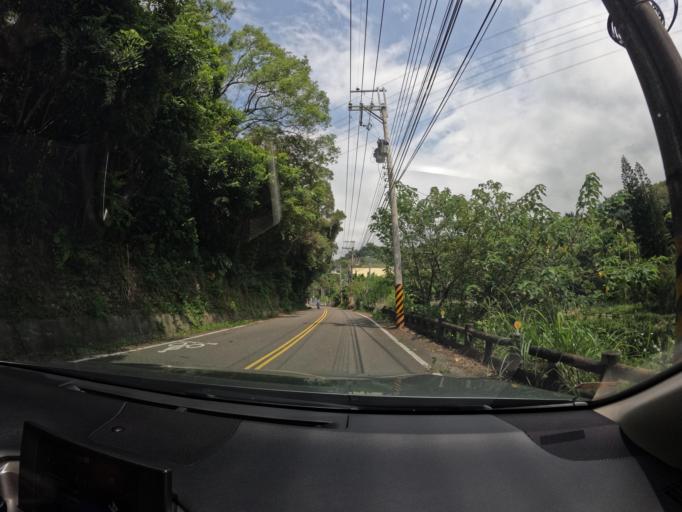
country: TW
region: Taiwan
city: Fengyuan
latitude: 24.3091
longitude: 120.8552
